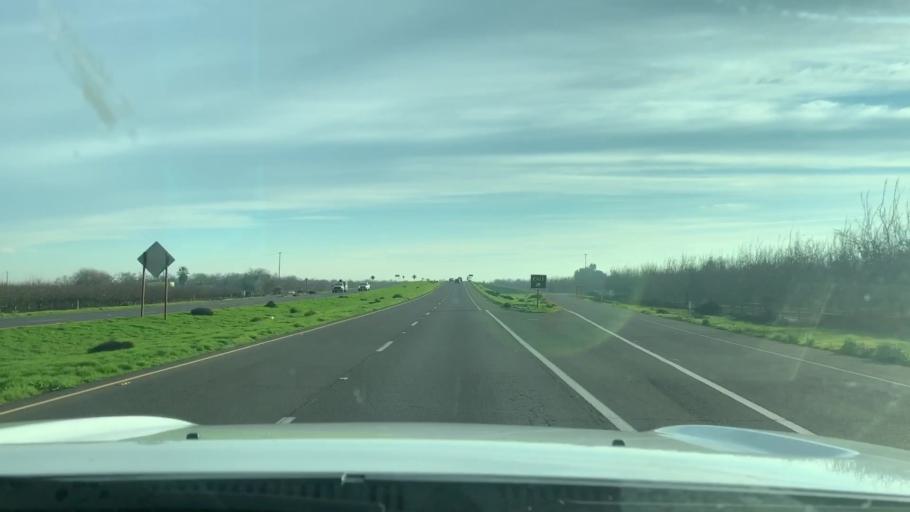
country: US
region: California
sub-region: Fresno County
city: Riverdale
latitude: 36.4054
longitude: -119.8065
